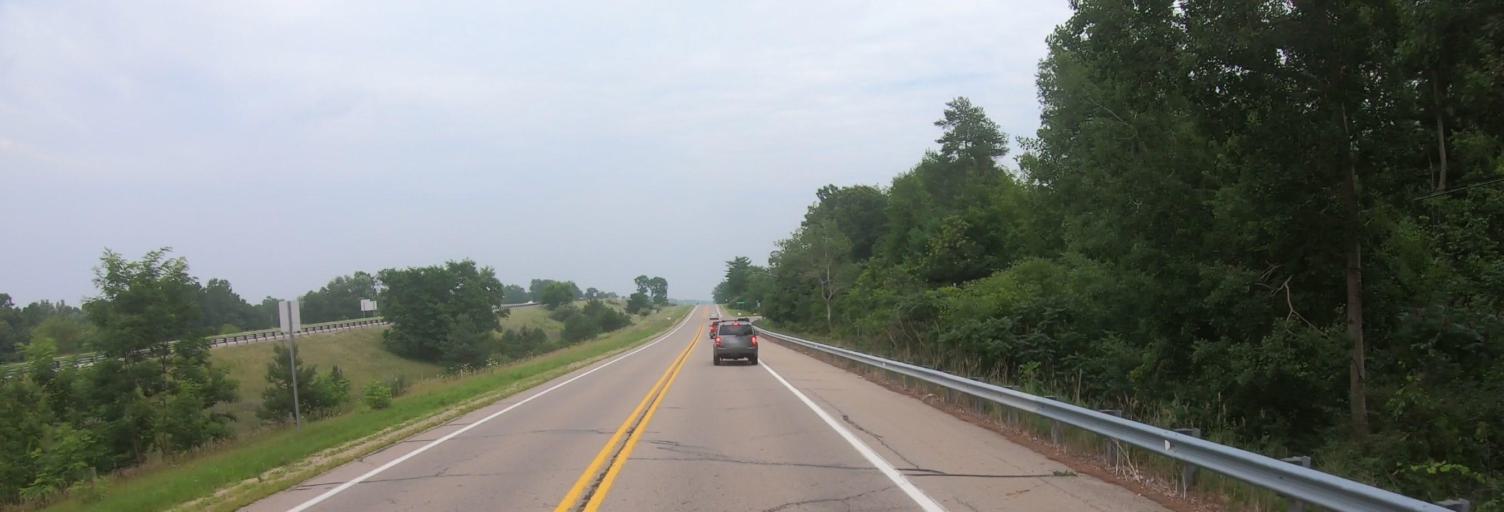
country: US
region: Michigan
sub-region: Shiawassee County
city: Laingsburg
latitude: 42.8047
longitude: -84.3269
